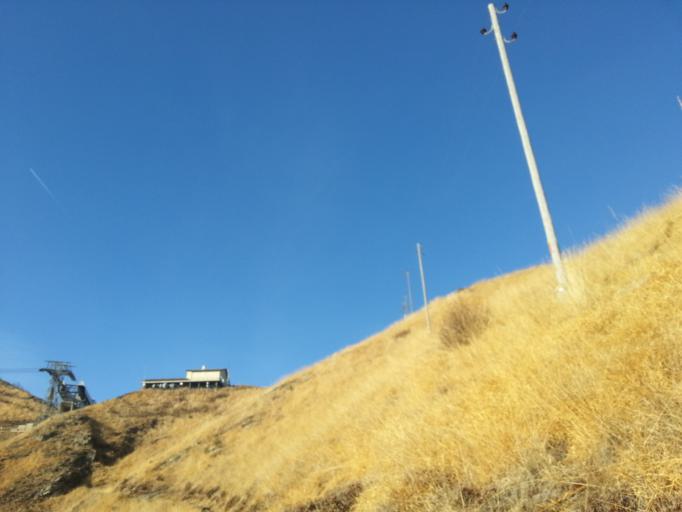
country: IT
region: Lombardy
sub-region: Provincia di Varese
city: Curiglia
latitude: 46.0395
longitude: 8.8374
